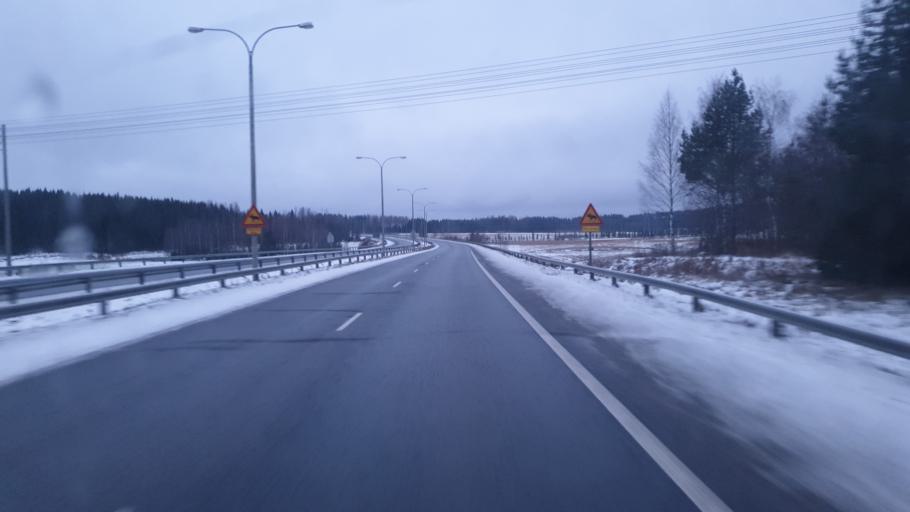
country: FI
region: Northern Savo
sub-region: Kuopio
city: Siilinjaervi
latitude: 63.0520
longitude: 27.6684
